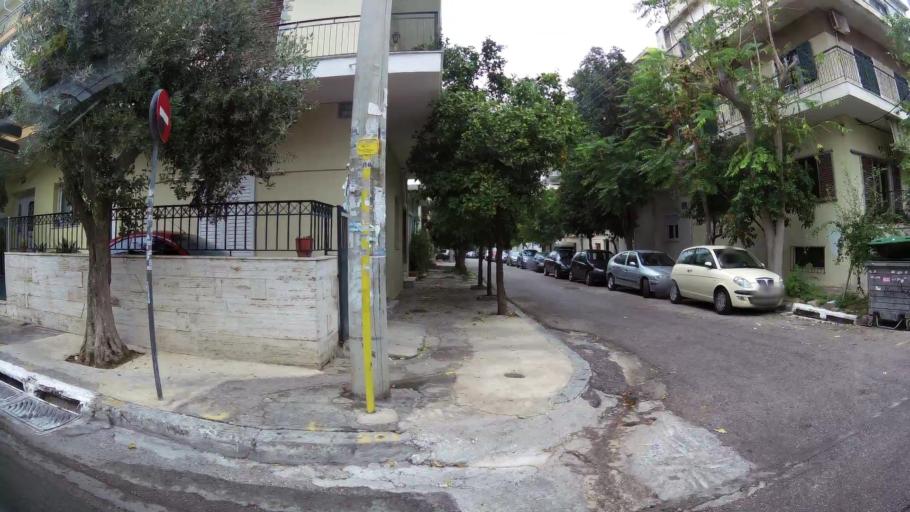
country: GR
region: Attica
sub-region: Nomarchia Athinas
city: Agia Varvara
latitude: 37.9814
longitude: 23.6588
